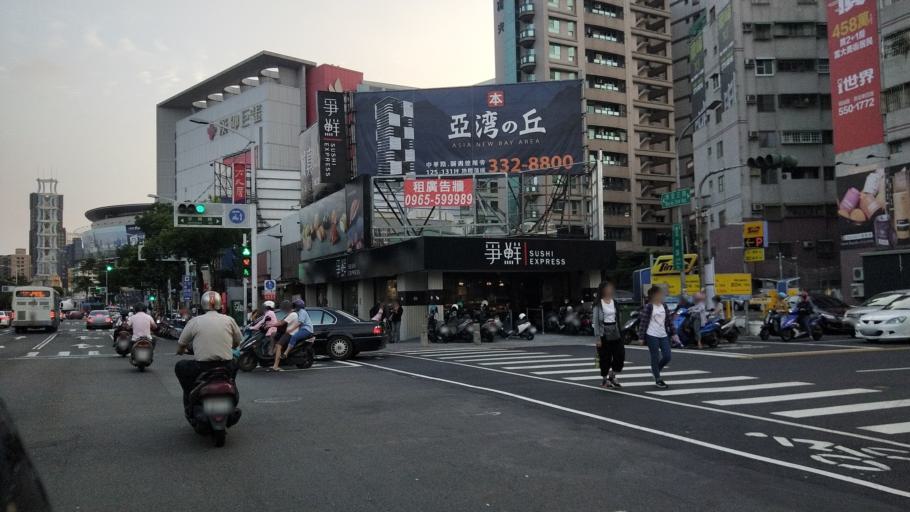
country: TW
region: Kaohsiung
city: Kaohsiung
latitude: 22.6715
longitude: 120.3038
